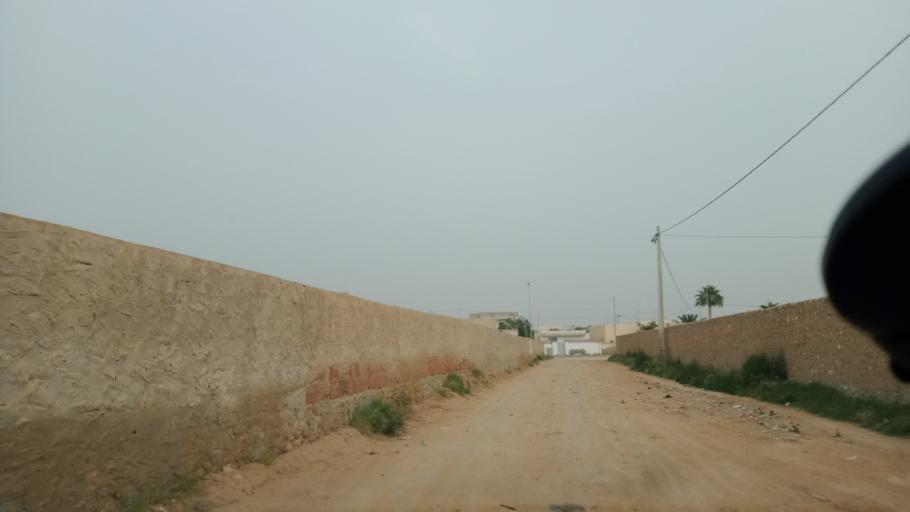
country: TN
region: Safaqis
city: Al Qarmadah
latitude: 34.7933
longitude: 10.7679
